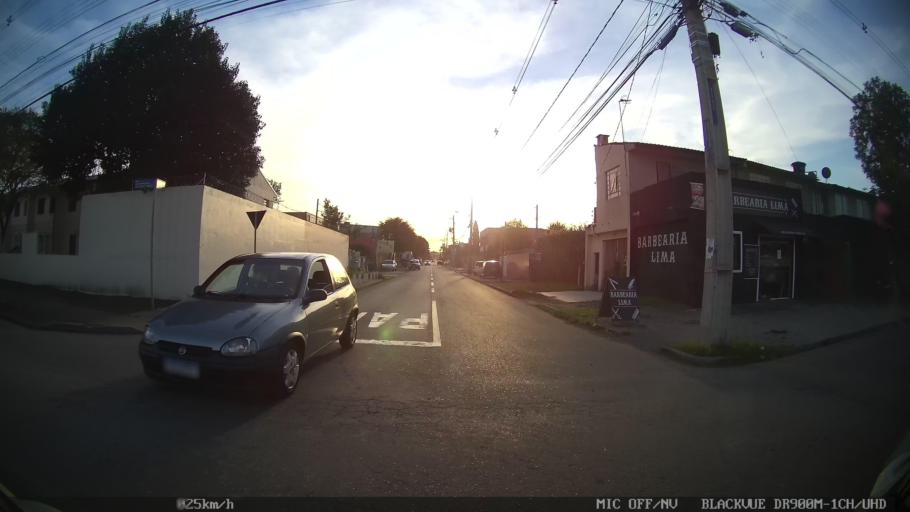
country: BR
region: Parana
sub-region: Pinhais
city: Pinhais
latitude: -25.4438
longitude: -49.1724
